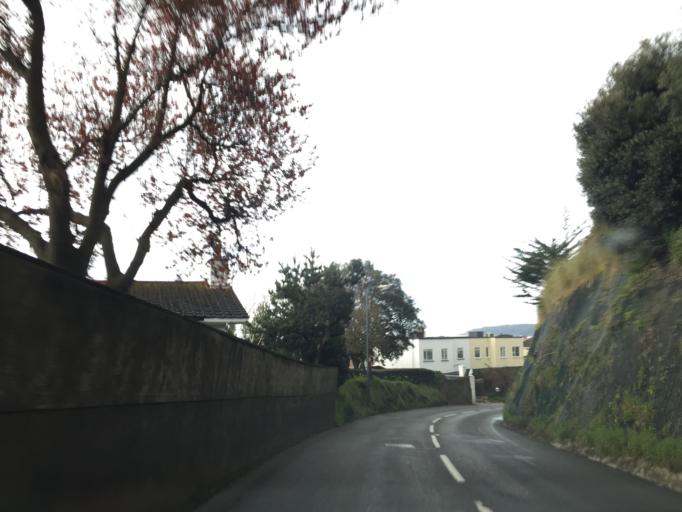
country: JE
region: St Helier
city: Saint Helier
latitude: 49.1998
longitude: -2.1370
